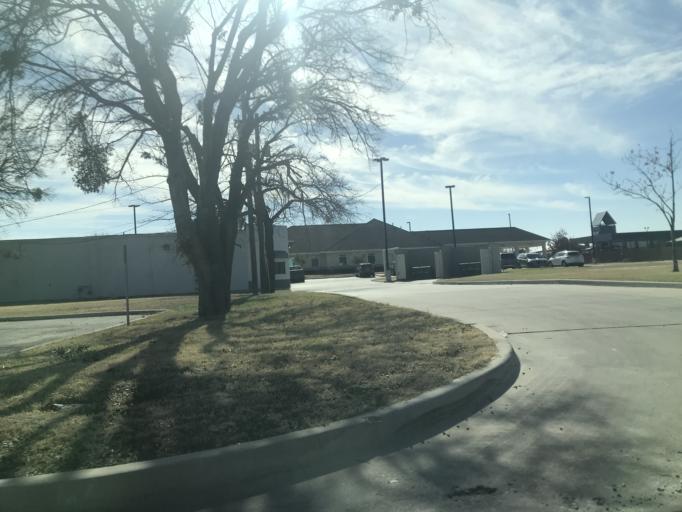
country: US
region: Texas
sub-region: Taylor County
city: Abilene
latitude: 32.4191
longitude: -99.7504
